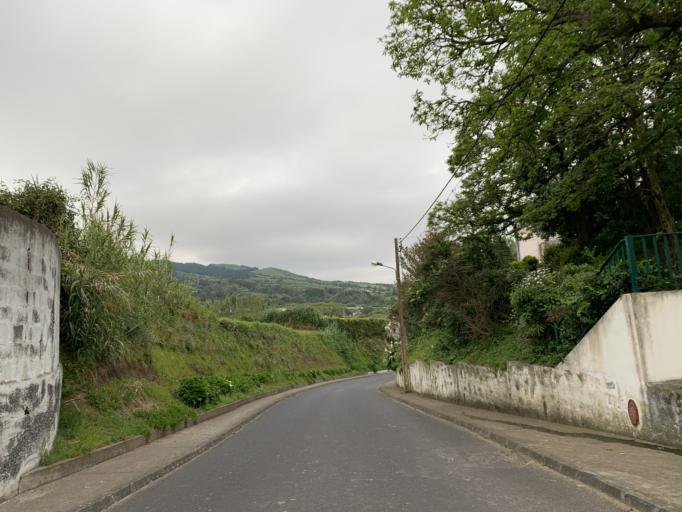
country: PT
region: Azores
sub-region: Ponta Delgada
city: Arrifes
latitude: 37.8482
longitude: -25.8411
